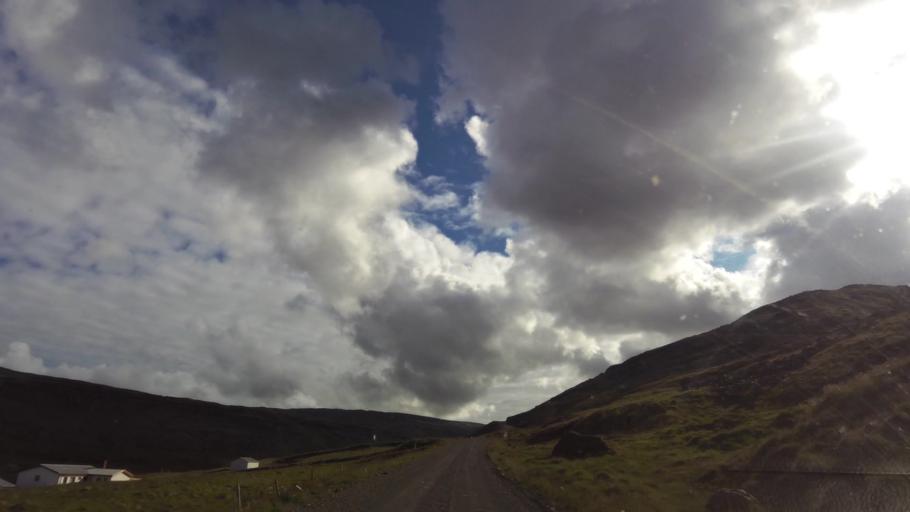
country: IS
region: West
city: Olafsvik
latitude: 65.5645
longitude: -24.1762
